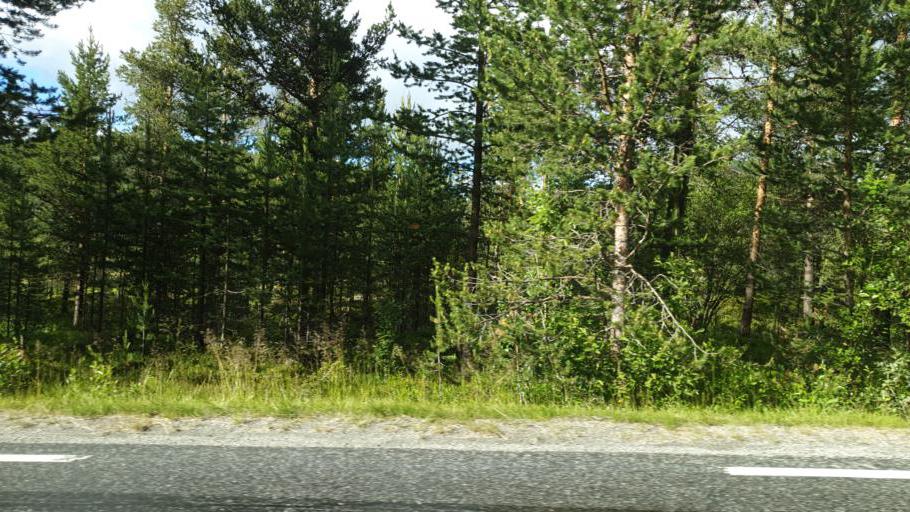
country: NO
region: Oppland
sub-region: Vaga
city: Vagamo
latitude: 61.8217
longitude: 8.9774
